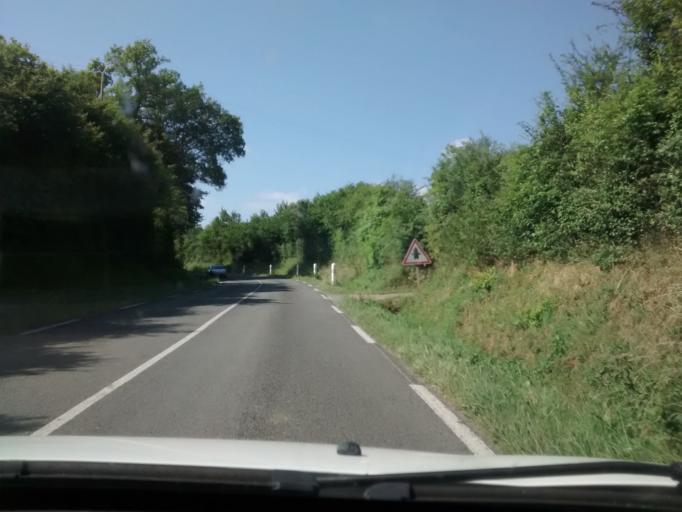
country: FR
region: Pays de la Loire
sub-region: Departement de la Sarthe
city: Vibraye
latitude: 47.9916
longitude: 0.7629
